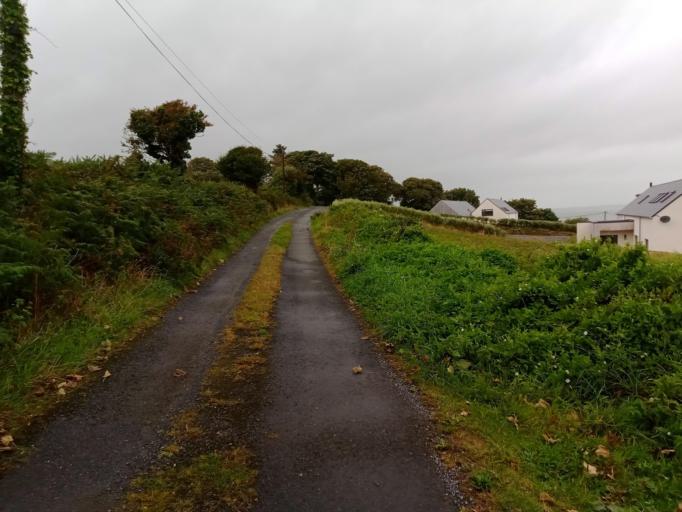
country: IE
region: Munster
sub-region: Waterford
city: Dungarvan
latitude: 52.0537
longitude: -7.5418
